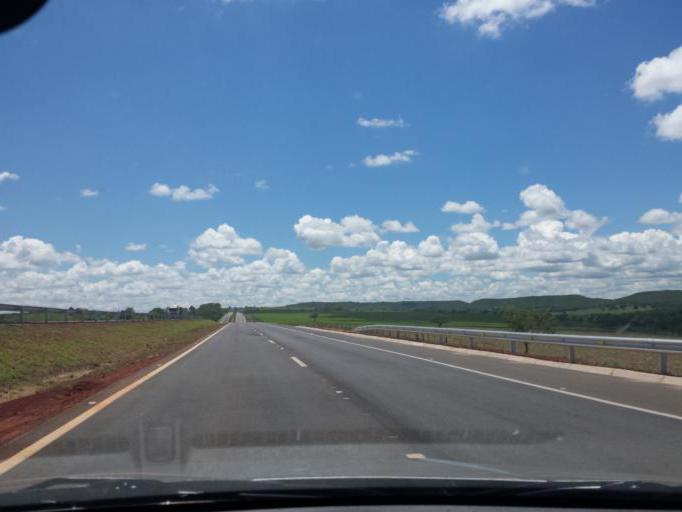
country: BR
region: Goias
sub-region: Cristalina
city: Cristalina
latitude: -16.6052
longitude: -47.7699
